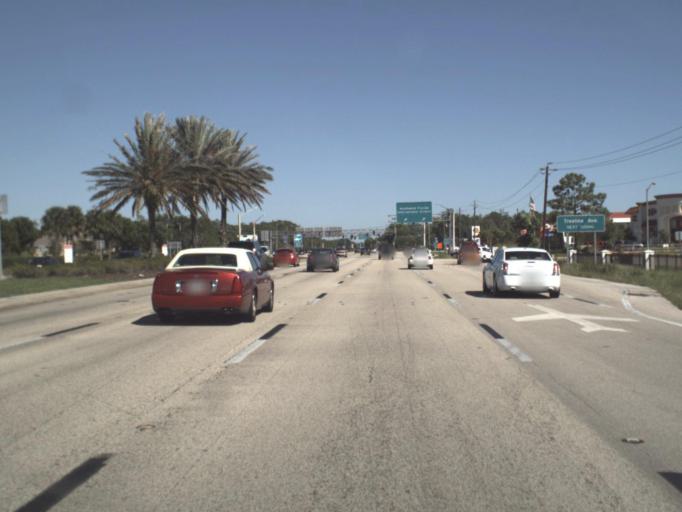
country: US
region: Florida
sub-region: Lee County
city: Gateway
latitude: 26.5472
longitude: -81.7896
